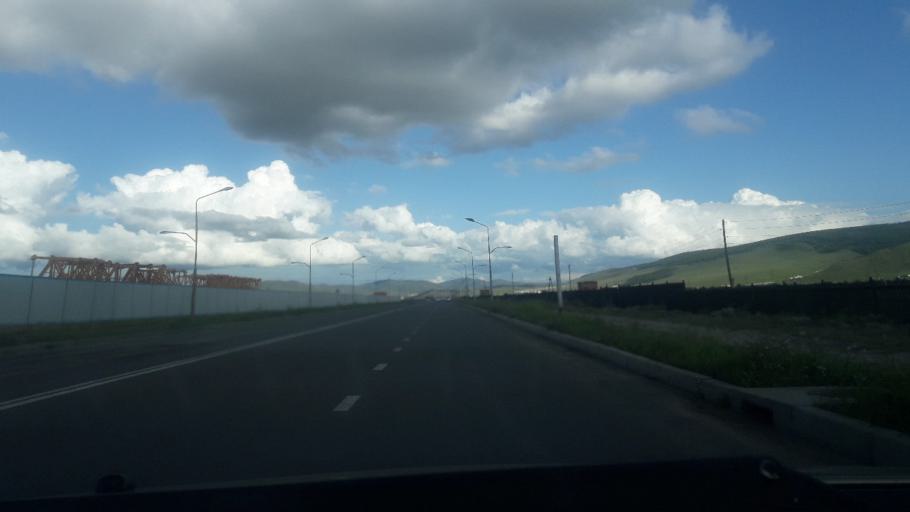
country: MN
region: Ulaanbaatar
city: Ulaanbaatar
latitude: 47.9052
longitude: 106.9723
